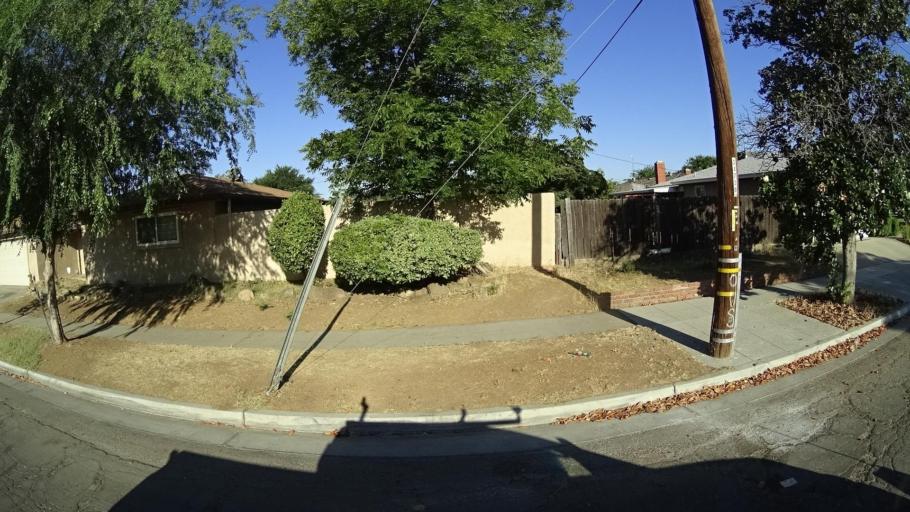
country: US
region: California
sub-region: Fresno County
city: Fresno
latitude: 36.7749
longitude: -119.8321
